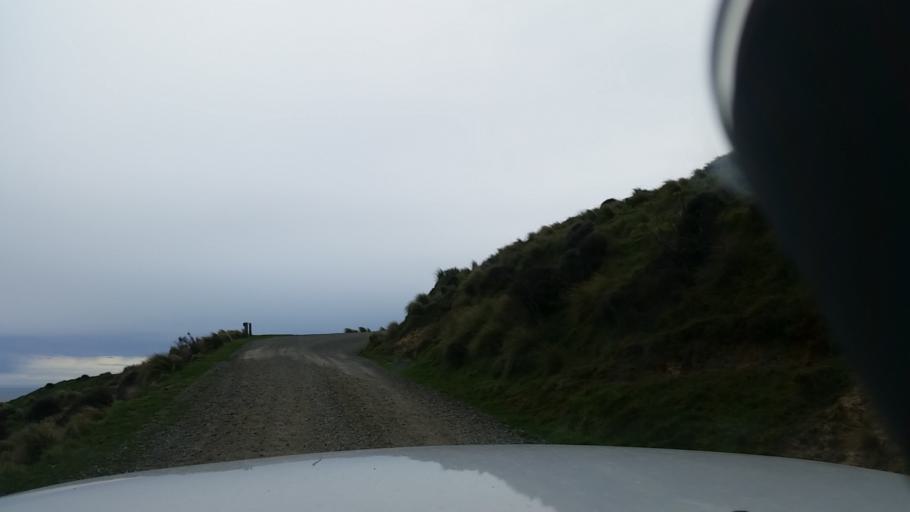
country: NZ
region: Canterbury
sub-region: Christchurch City
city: Christchurch
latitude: -43.8557
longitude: 172.7650
